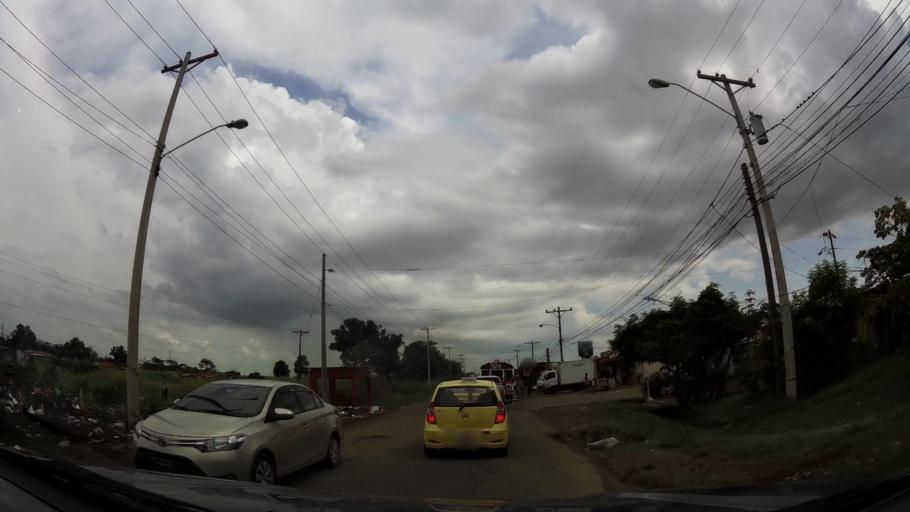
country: PA
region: Panama
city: Cabra Numero Uno
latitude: 9.1114
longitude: -79.3239
